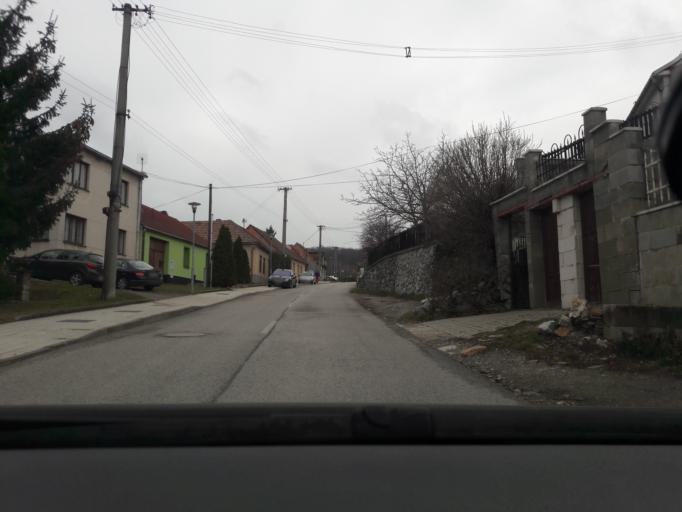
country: SK
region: Bratislavsky
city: Modra
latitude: 48.3948
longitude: 17.3508
